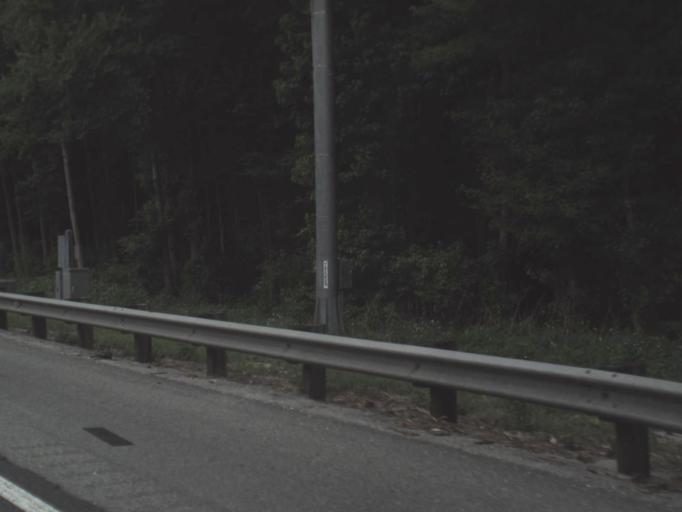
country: US
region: Florida
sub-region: Saint Johns County
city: Palm Valley
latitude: 30.0864
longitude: -81.4977
